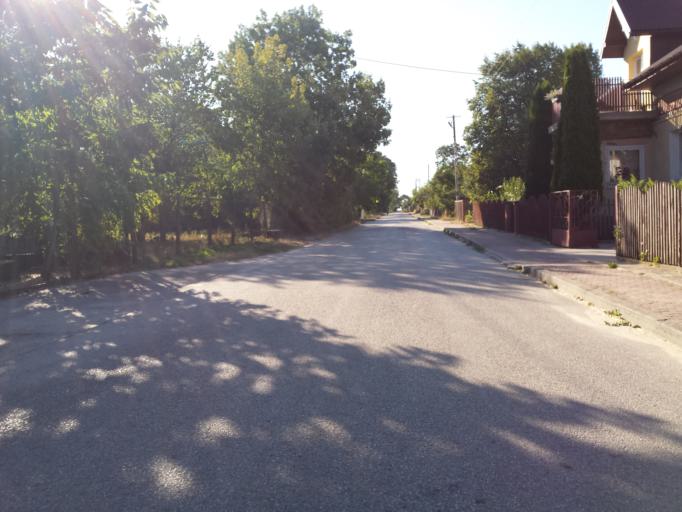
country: PL
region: Swietokrzyskie
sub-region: Powiat buski
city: Gnojno
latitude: 50.6486
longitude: 20.8174
